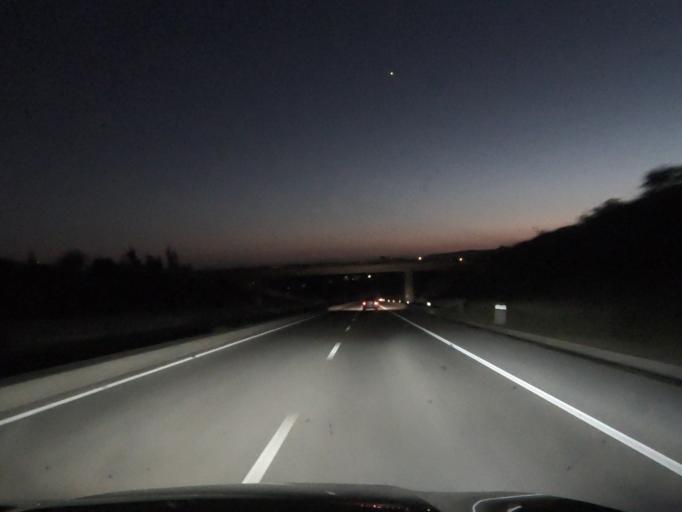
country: PT
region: Faro
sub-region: Loule
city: Loule
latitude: 37.1452
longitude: -8.0281
